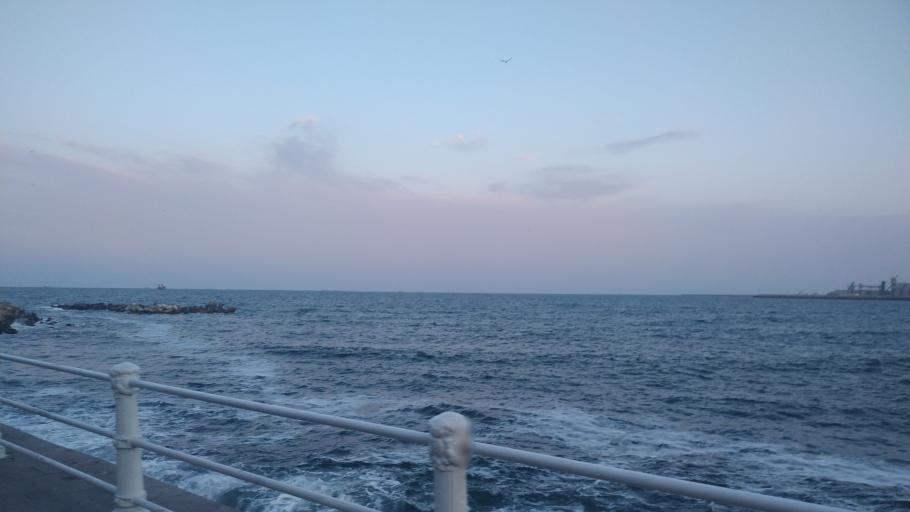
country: RO
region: Constanta
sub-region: Municipiul Constanta
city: Constanta
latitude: 44.1701
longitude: 28.6613
